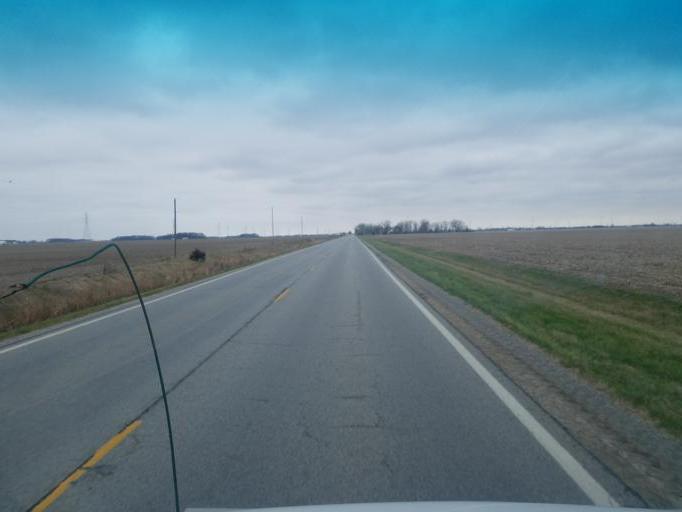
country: US
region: Ohio
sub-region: Van Wert County
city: Van Wert
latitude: 40.9321
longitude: -84.4593
